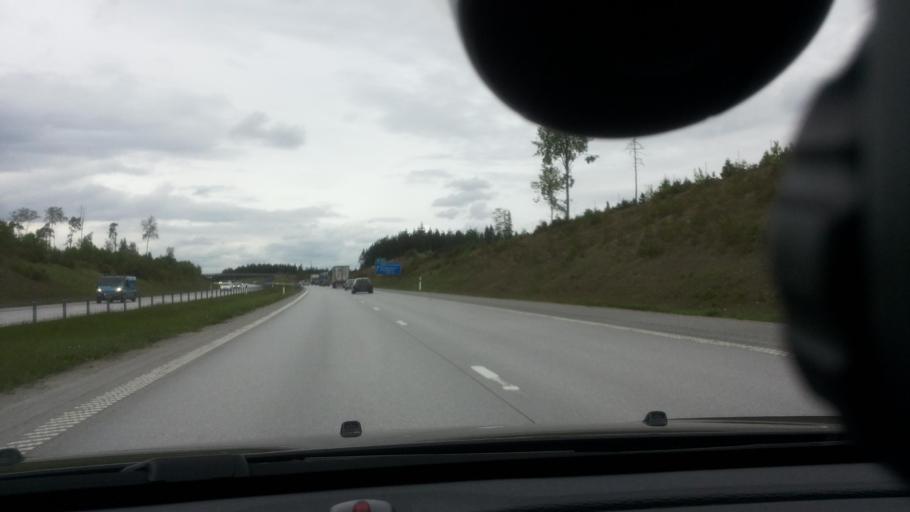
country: SE
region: Uppsala
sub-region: Uppsala Kommun
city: Gamla Uppsala
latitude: 59.9270
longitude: 17.6586
